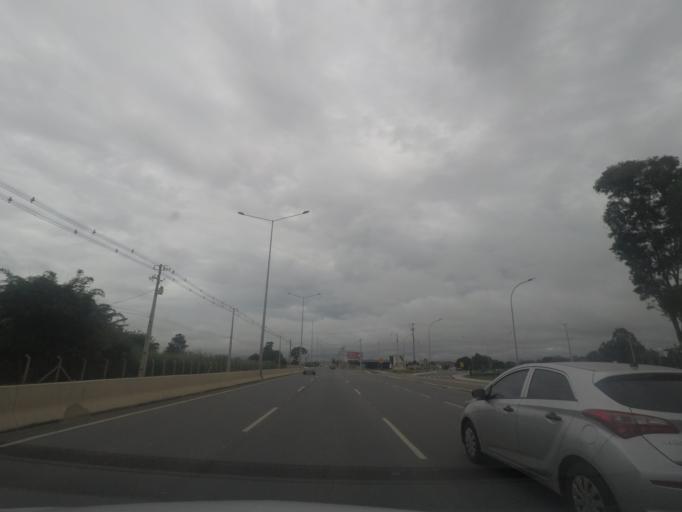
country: BR
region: Parana
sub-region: Pinhais
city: Pinhais
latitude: -25.4419
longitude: -49.1501
